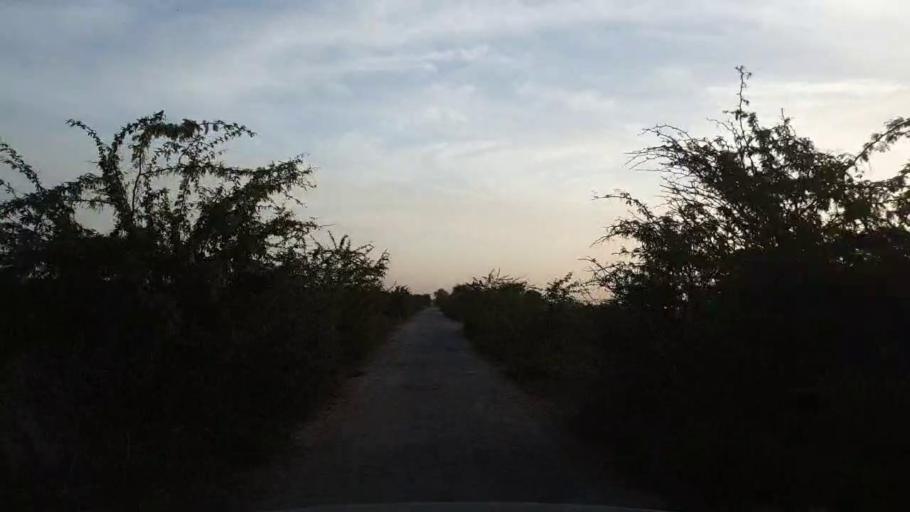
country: PK
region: Sindh
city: Kunri
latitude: 25.1148
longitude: 69.5643
